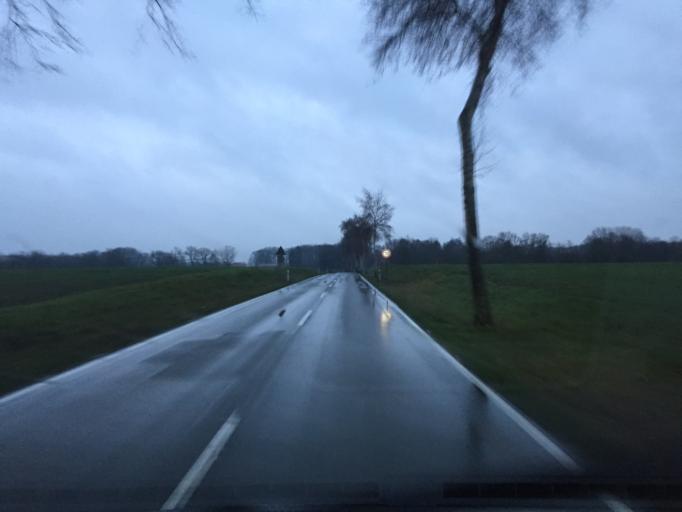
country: DE
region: Lower Saxony
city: Sustedt
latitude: 52.8963
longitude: 8.9087
